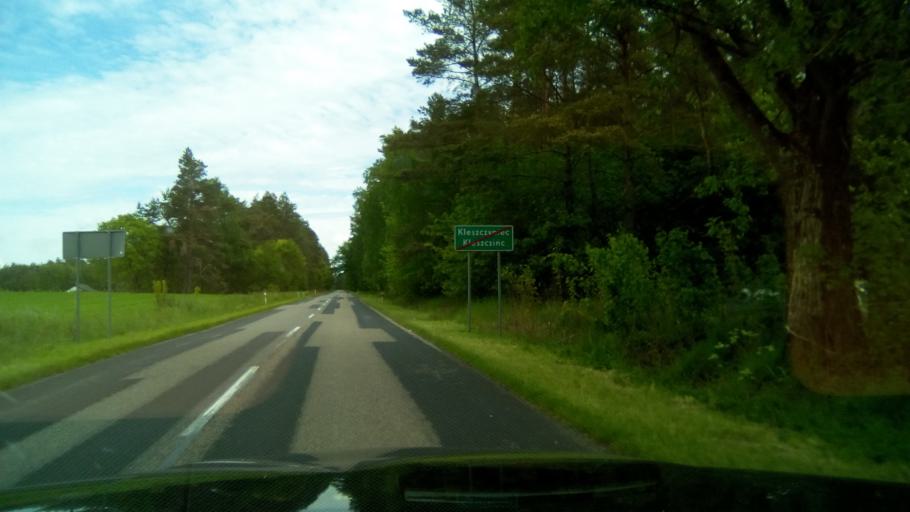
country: PL
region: Pomeranian Voivodeship
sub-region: Powiat bytowski
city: Czarna Dabrowka
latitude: 54.3381
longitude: 17.5441
